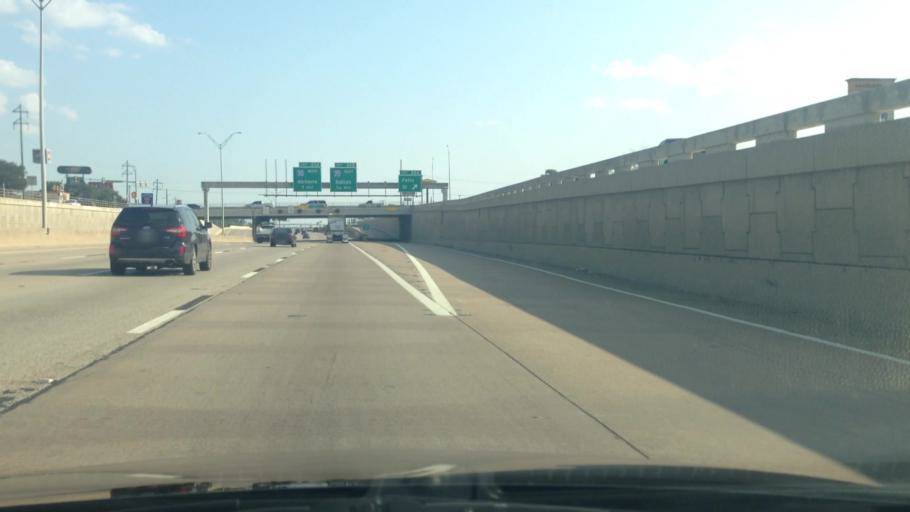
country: US
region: Texas
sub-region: Tarrant County
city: Edgecliff Village
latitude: 32.6862
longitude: -97.3208
